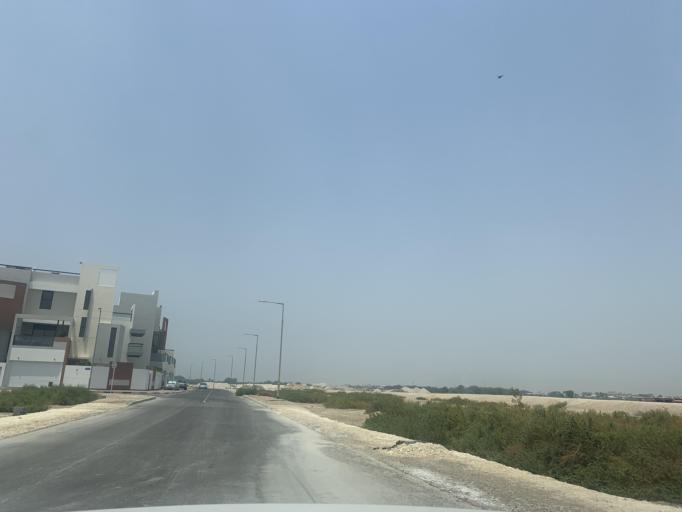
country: BH
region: Central Governorate
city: Madinat Hamad
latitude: 26.1325
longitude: 50.4701
